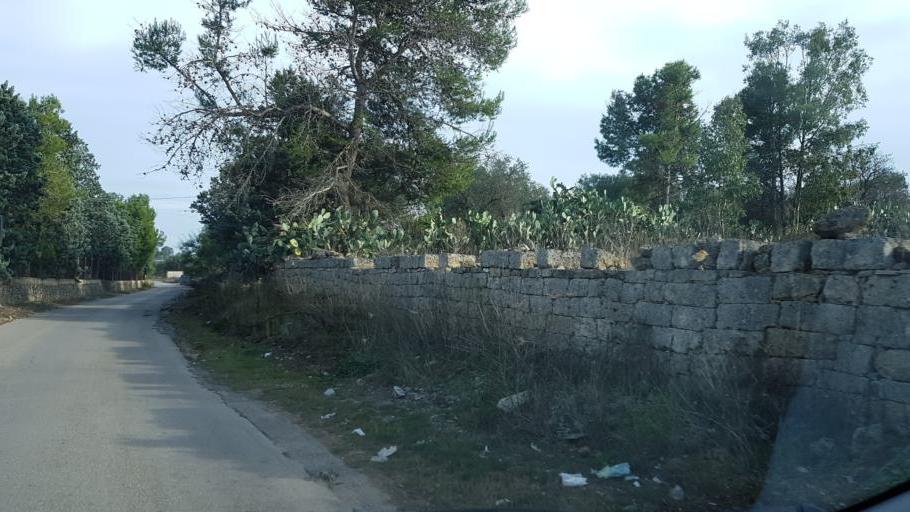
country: IT
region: Apulia
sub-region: Provincia di Brindisi
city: Oria
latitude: 40.5000
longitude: 17.6547
